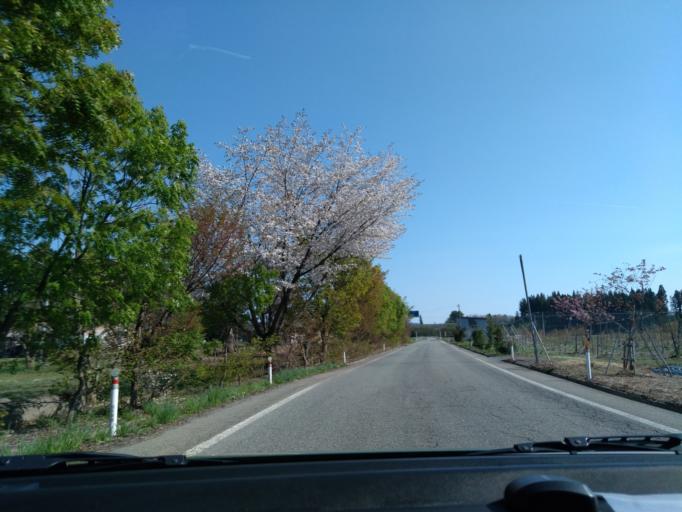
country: JP
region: Akita
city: Yokotemachi
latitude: 39.3561
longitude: 140.5706
